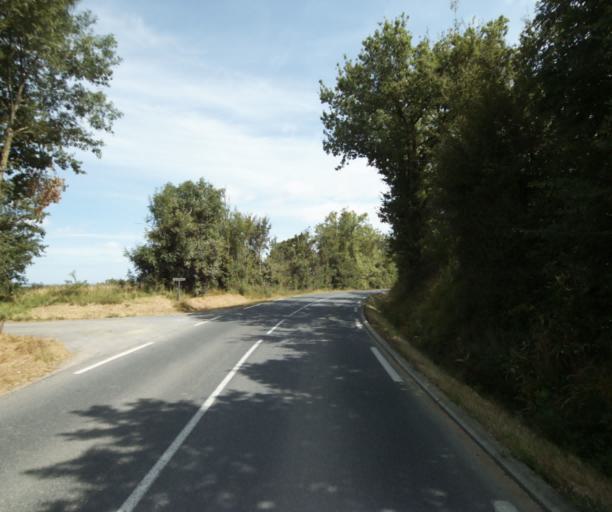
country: FR
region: Midi-Pyrenees
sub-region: Departement du Tarn
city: Dourgne
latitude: 43.4728
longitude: 2.1048
